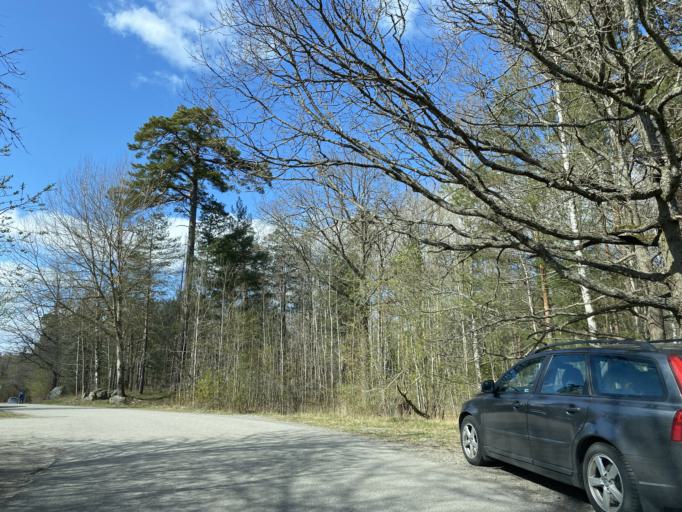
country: SE
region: Stockholm
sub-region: Nacka Kommun
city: Nacka
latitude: 59.3299
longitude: 18.1492
